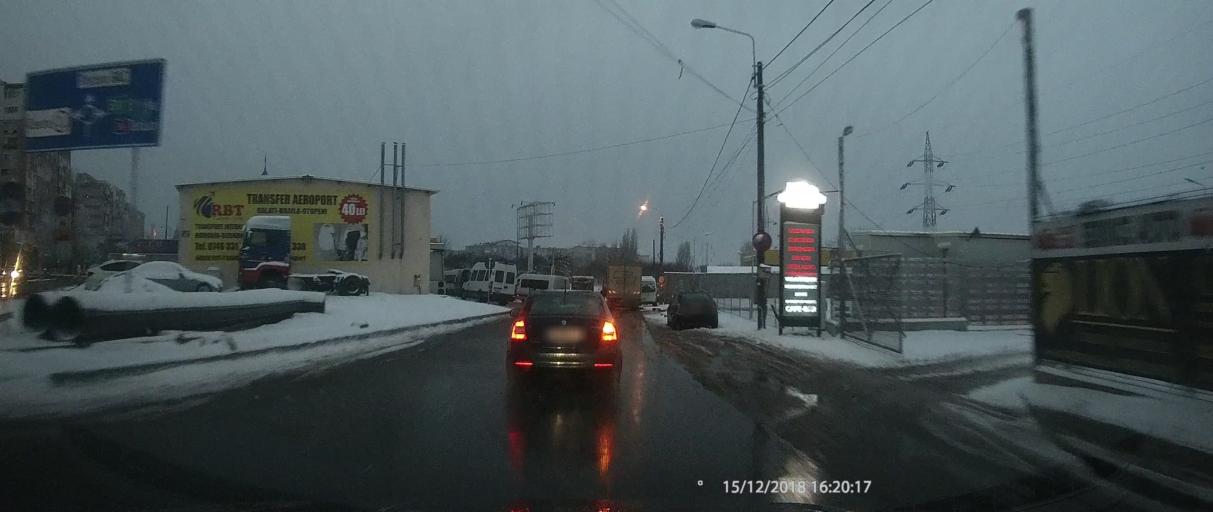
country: RO
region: Galati
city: Galati
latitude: 45.4143
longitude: 28.0050
